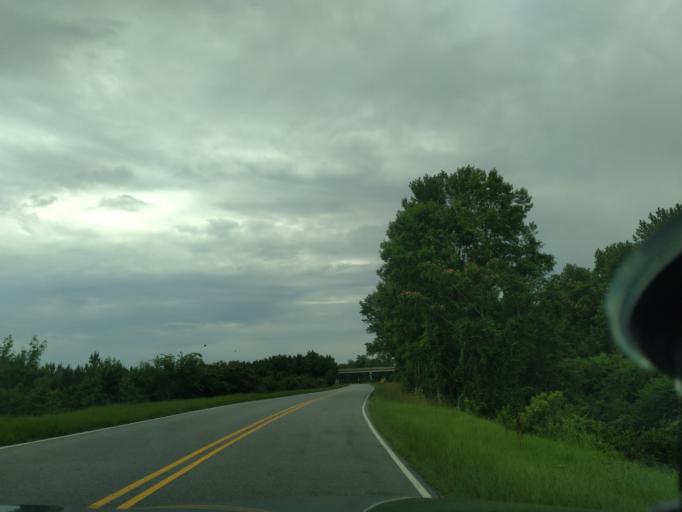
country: US
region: North Carolina
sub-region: Washington County
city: Plymouth
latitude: 35.8761
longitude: -76.6001
